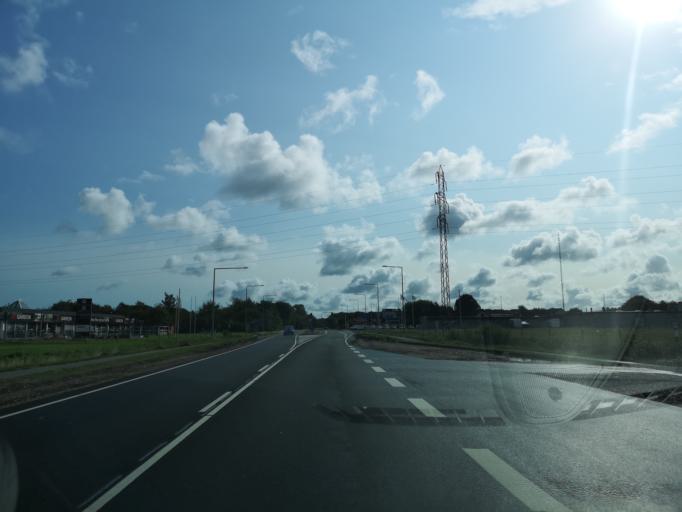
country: DK
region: Central Jutland
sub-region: Herning Kommune
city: Snejbjerg
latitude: 56.1349
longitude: 8.9286
